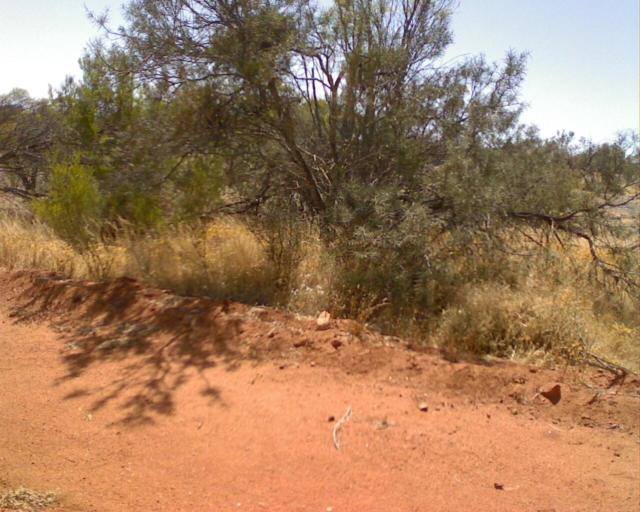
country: AU
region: Western Australia
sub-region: Wongan-Ballidu
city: Wongan Hills
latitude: -30.4238
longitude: 116.9675
